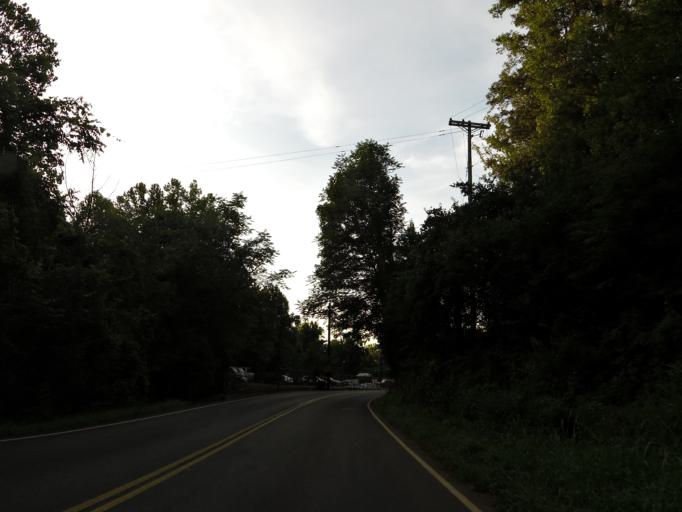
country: US
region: Tennessee
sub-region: Knox County
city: Knoxville
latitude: 35.9426
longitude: -83.9192
